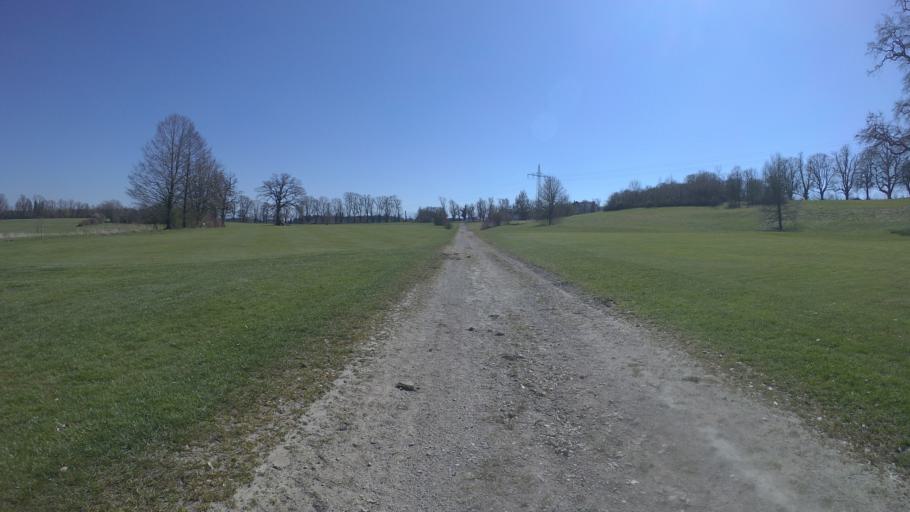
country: DE
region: Bavaria
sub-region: Upper Bavaria
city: Chieming
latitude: 47.9271
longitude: 12.5082
